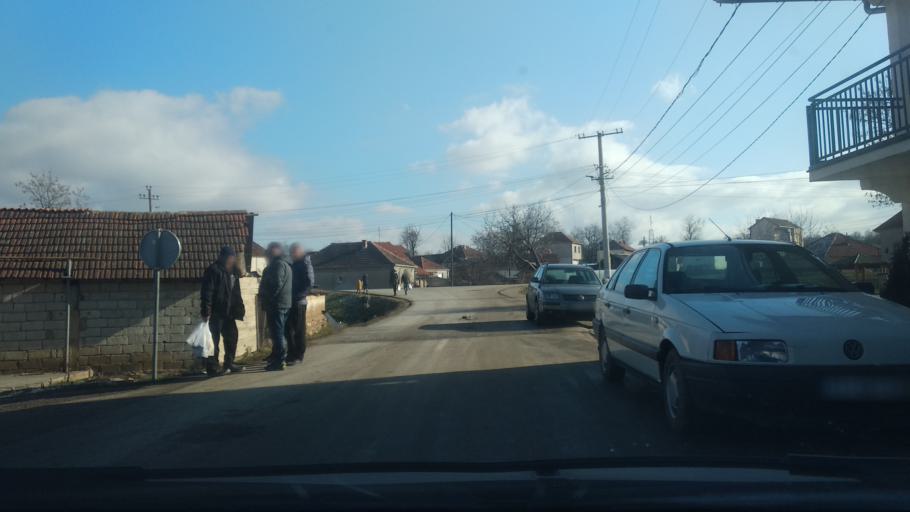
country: XK
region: Pristina
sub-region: Lipjan
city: Lipljan
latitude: 42.5461
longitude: 21.1807
